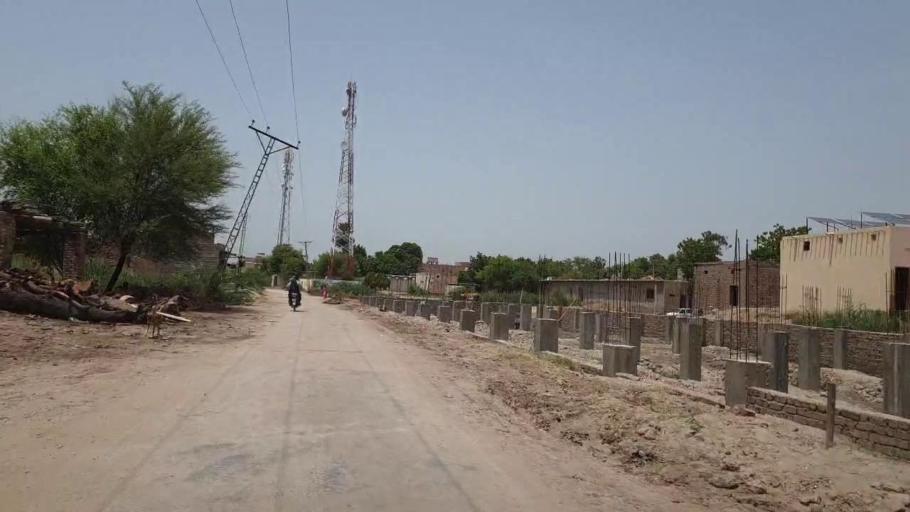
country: PK
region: Sindh
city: Daur
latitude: 26.3980
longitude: 68.4387
